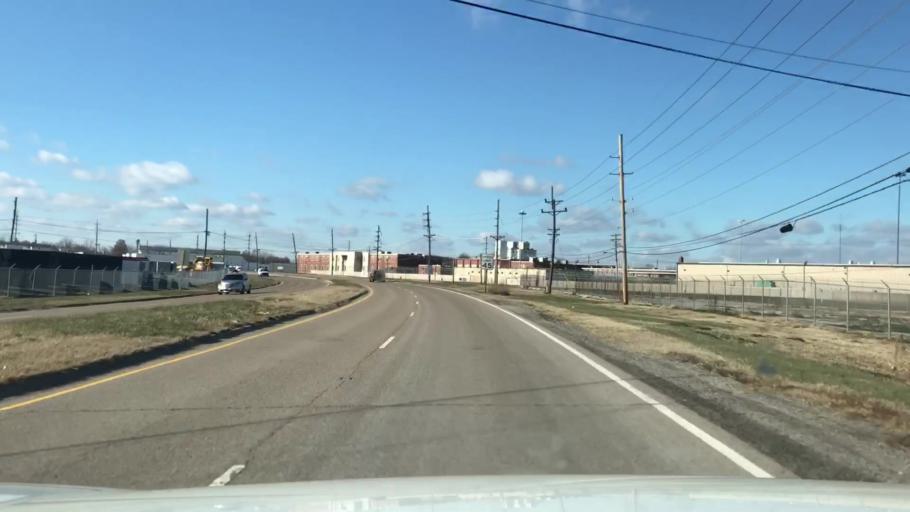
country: US
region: Illinois
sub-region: Saint Clair County
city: Washington Park
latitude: 38.6149
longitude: -90.0885
